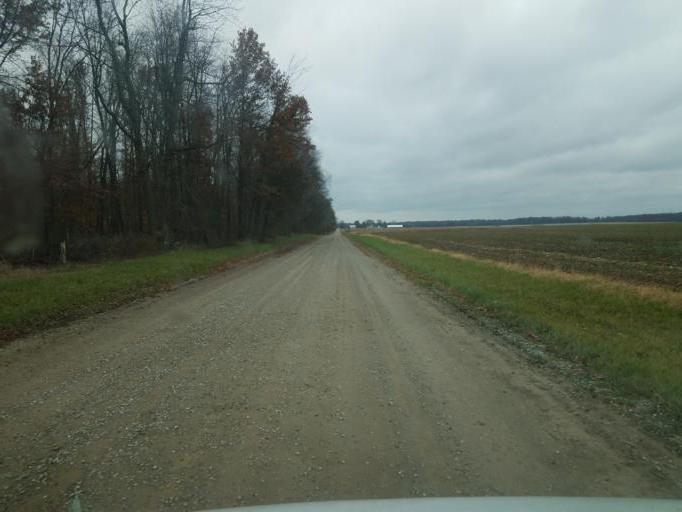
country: US
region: Ohio
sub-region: Licking County
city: Johnstown
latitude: 40.2208
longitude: -82.6753
